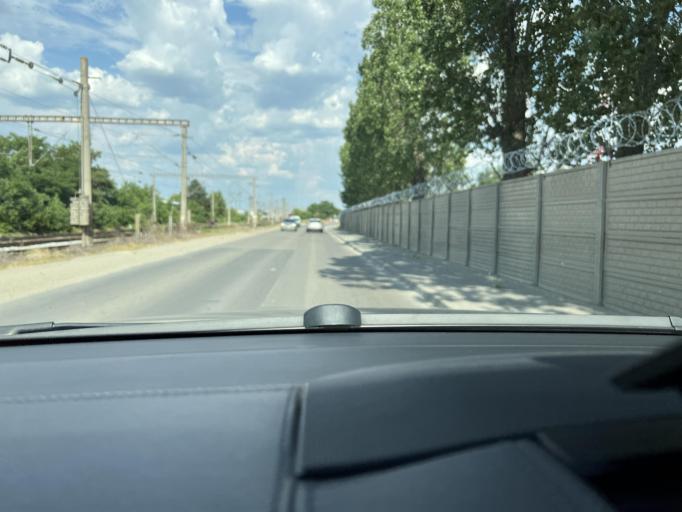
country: RO
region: Cluj
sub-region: Municipiul Cluj-Napoca
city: Cluj-Napoca
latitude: 46.7783
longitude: 23.6617
